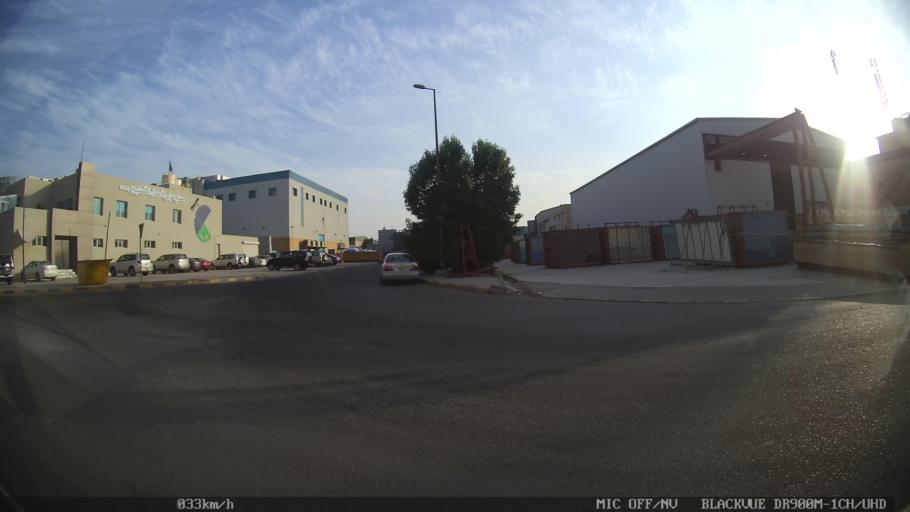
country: KW
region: Al Farwaniyah
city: Janub as Surrah
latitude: 29.2400
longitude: 48.0048
